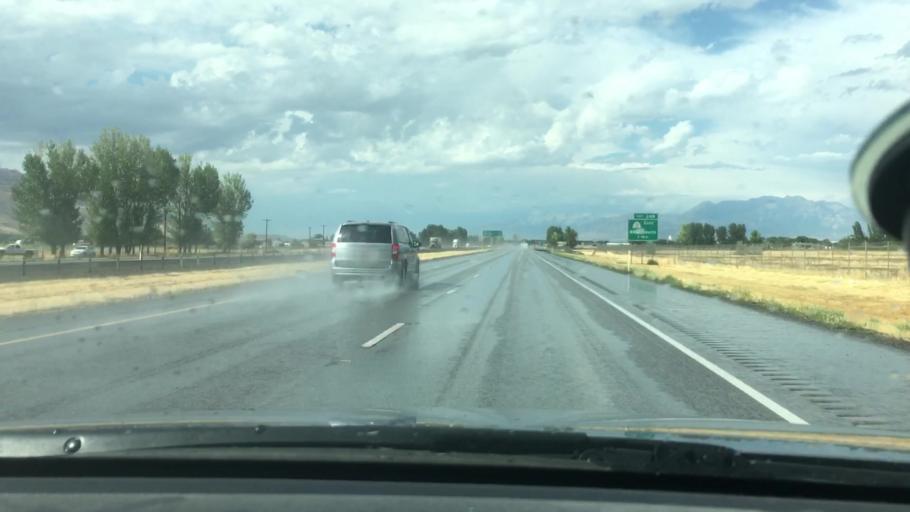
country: US
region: Utah
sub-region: Utah County
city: Payson
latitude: 40.0132
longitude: -111.7623
